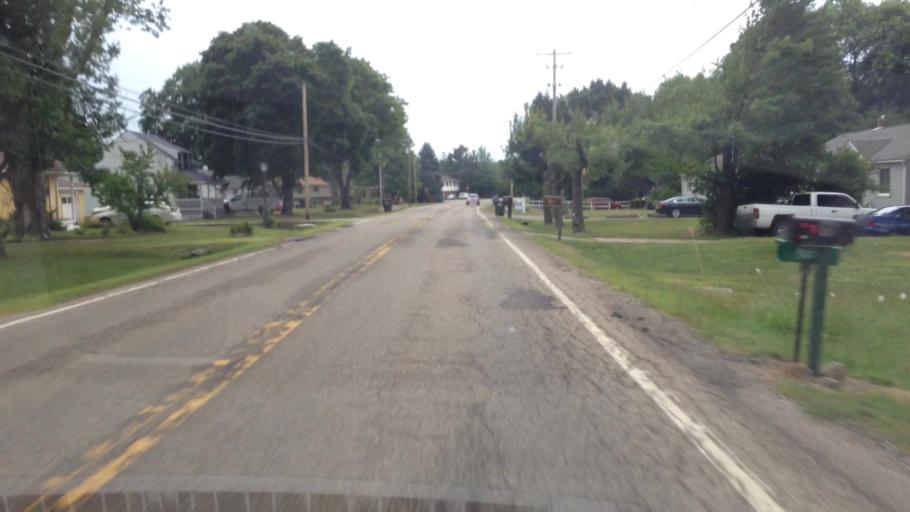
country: US
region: Ohio
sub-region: Stark County
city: Uniontown
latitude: 40.9797
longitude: -81.4416
